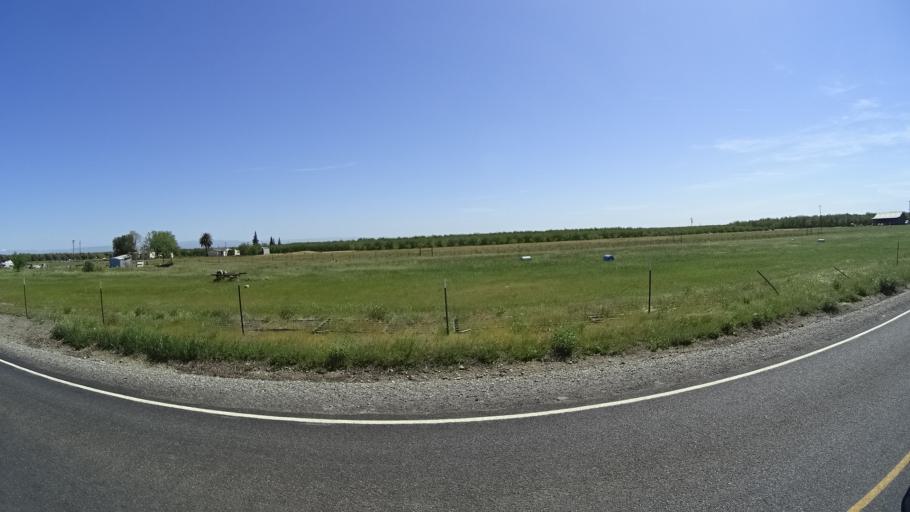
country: US
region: California
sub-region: Glenn County
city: Orland
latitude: 39.6798
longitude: -122.1406
